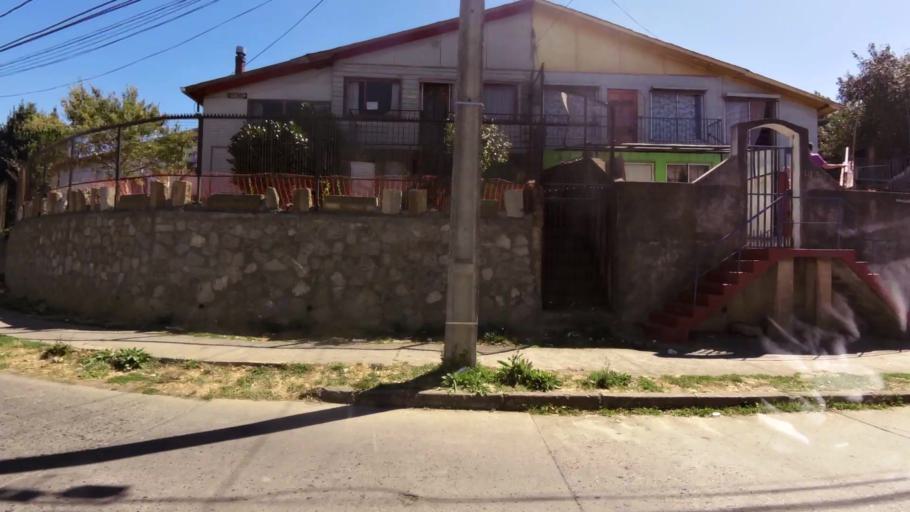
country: CL
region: Biobio
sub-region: Provincia de Concepcion
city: Penco
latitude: -36.7275
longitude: -72.9822
